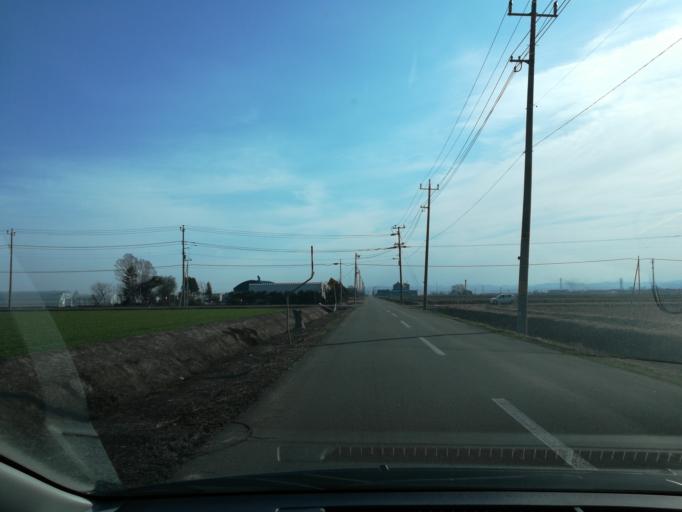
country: JP
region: Hokkaido
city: Ebetsu
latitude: 43.1597
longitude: 141.6471
